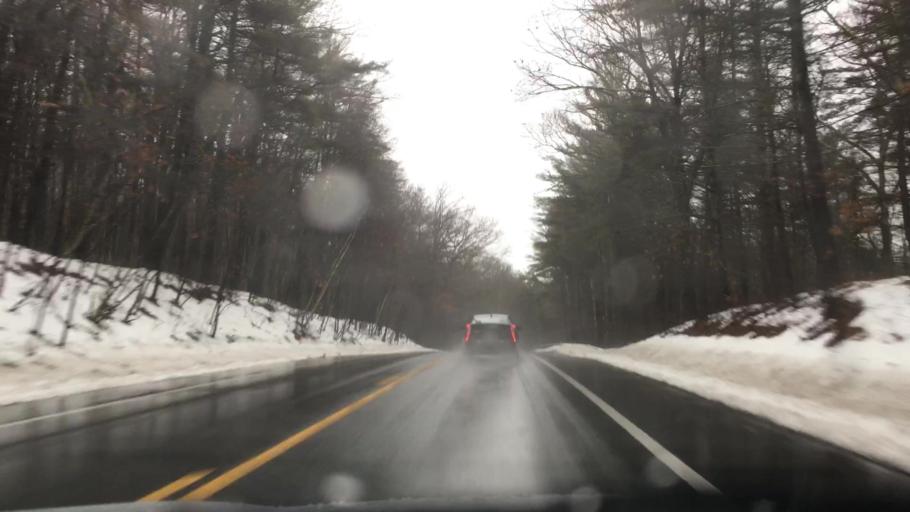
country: US
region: Massachusetts
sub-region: Franklin County
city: Shutesbury
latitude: 42.4324
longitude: -72.3960
